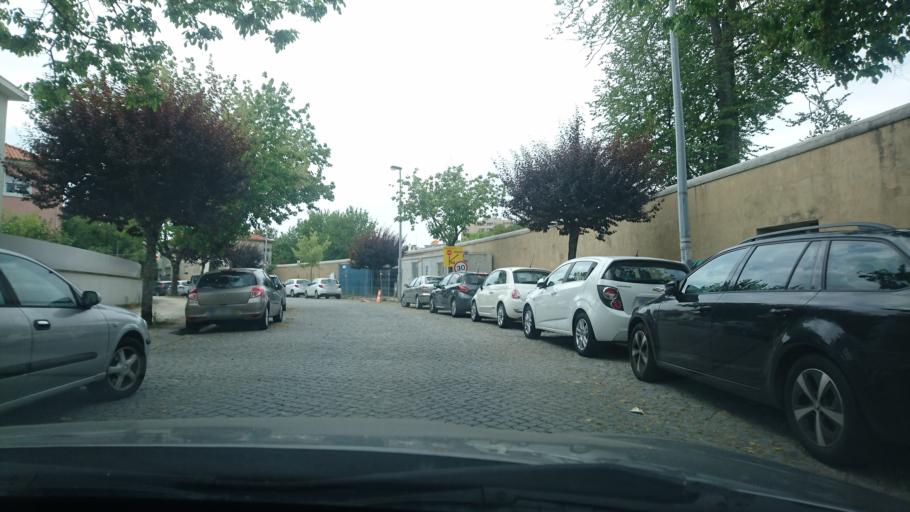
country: PT
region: Porto
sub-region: Porto
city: Porto
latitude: 41.1633
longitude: -8.5929
